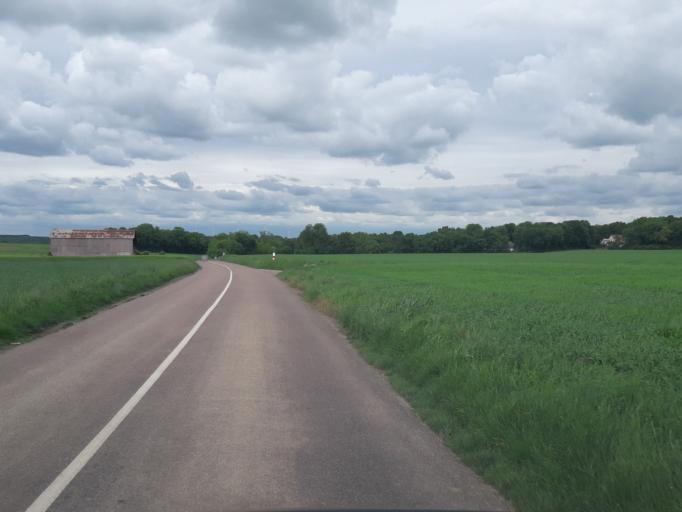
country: FR
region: Ile-de-France
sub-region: Departement de l'Essonne
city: Saclas
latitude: 48.3474
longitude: 2.1382
